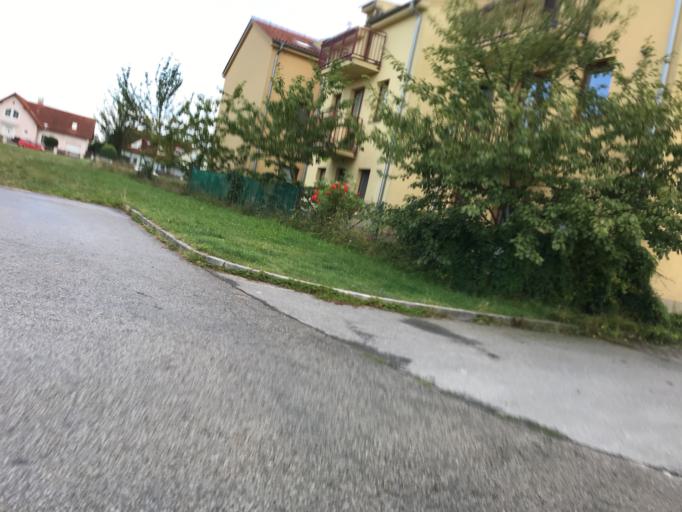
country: CZ
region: Jihocesky
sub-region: Okres Jindrichuv Hradec
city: Trebon
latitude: 49.0114
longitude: 14.7531
